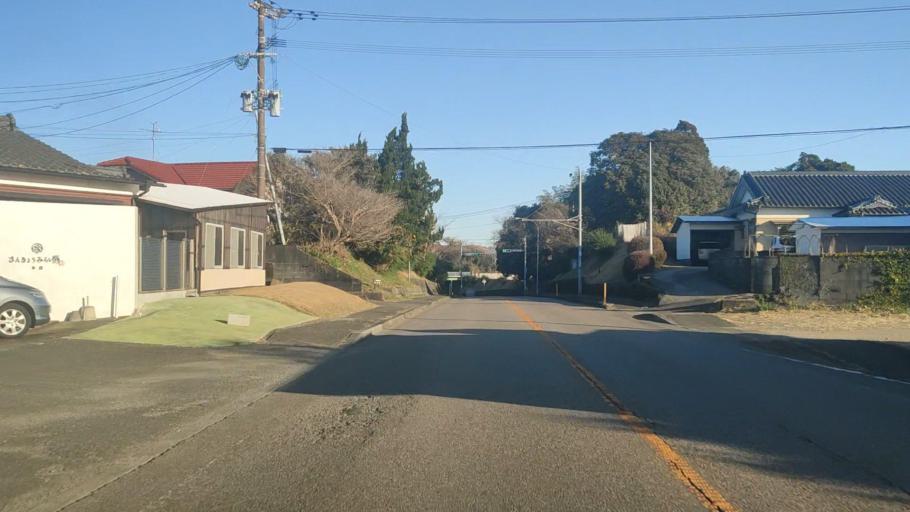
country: JP
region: Miyazaki
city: Takanabe
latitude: 32.2334
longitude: 131.5486
